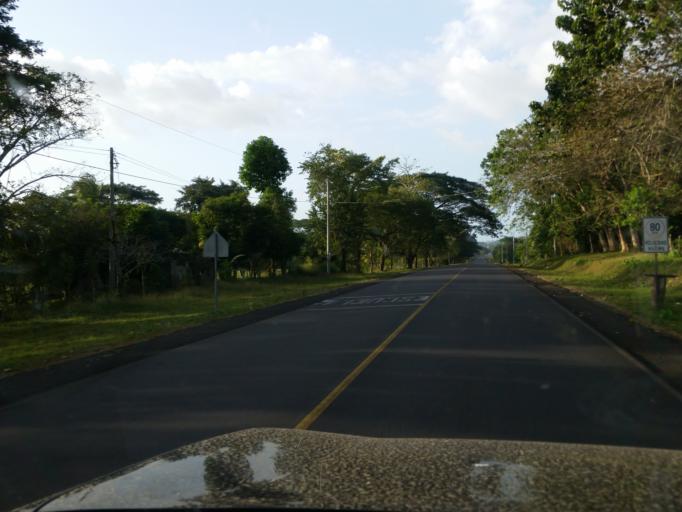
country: NI
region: Rio San Juan
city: San Miguelito
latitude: 11.3373
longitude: -84.7517
